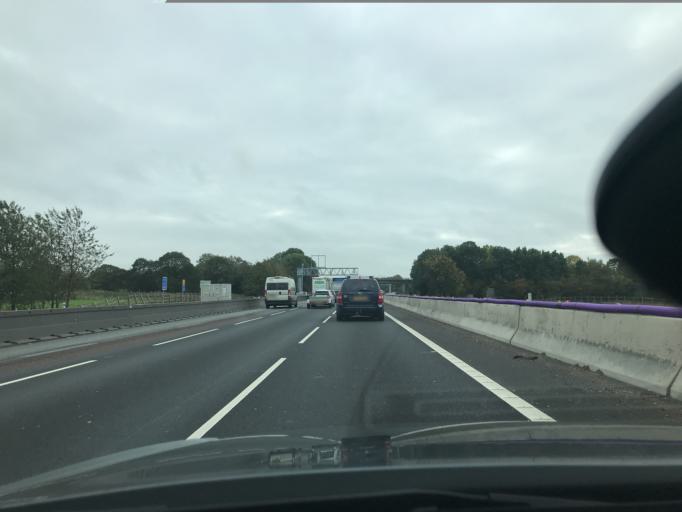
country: GB
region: England
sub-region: Cheshire East
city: Peover Superior
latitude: 53.2457
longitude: -2.4015
